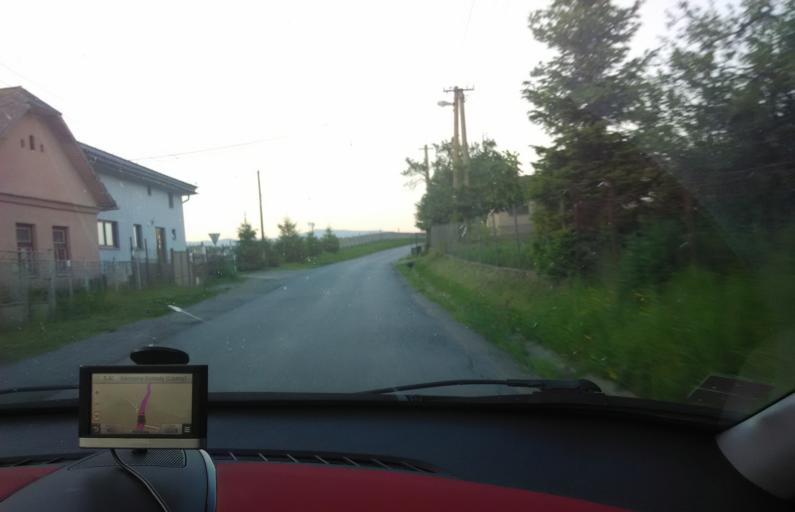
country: SK
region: Presovsky
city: Sabinov
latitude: 49.0626
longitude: 21.0642
